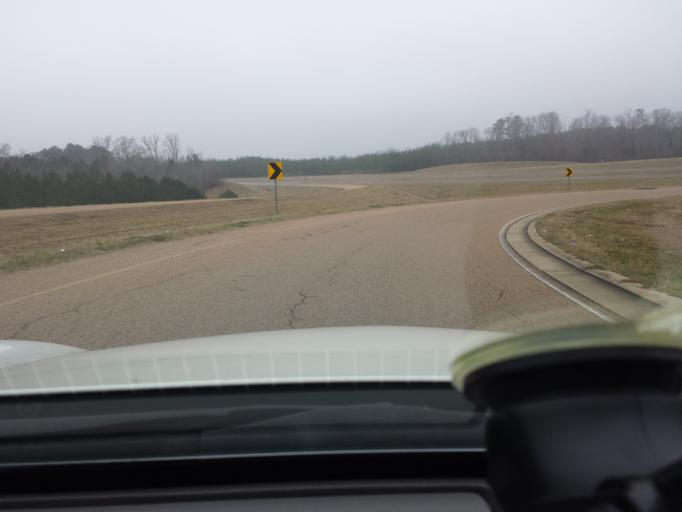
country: US
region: Mississippi
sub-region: Winston County
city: Louisville
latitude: 33.1571
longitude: -89.0892
